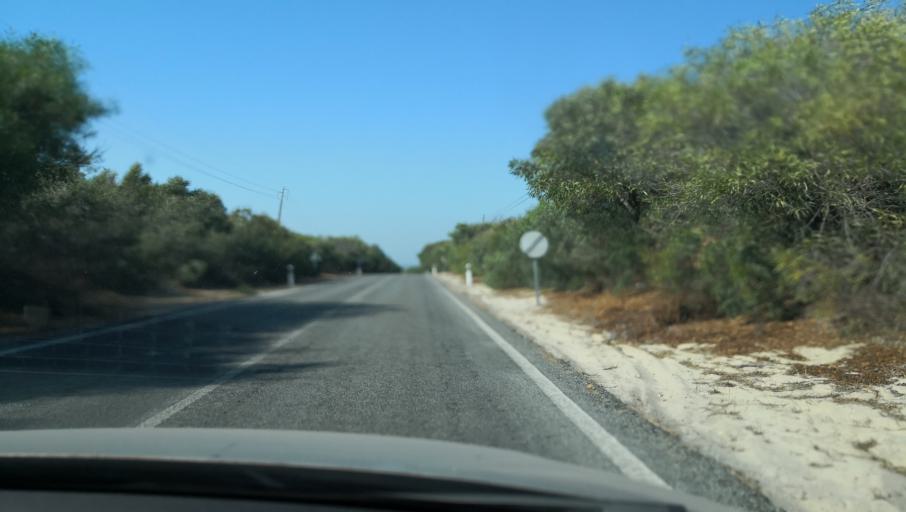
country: PT
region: Setubal
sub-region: Setubal
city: Setubal
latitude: 38.4133
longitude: -8.8148
